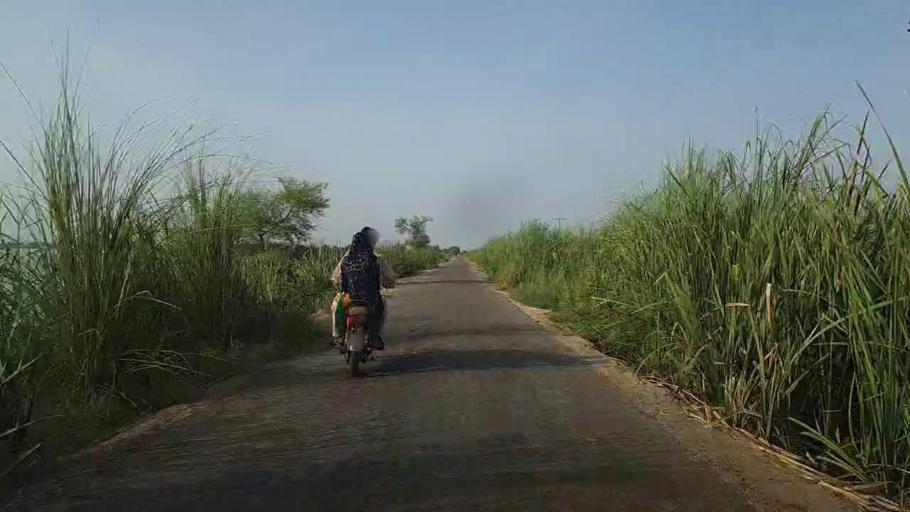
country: PK
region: Sindh
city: Khairpur
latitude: 28.0802
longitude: 69.8139
